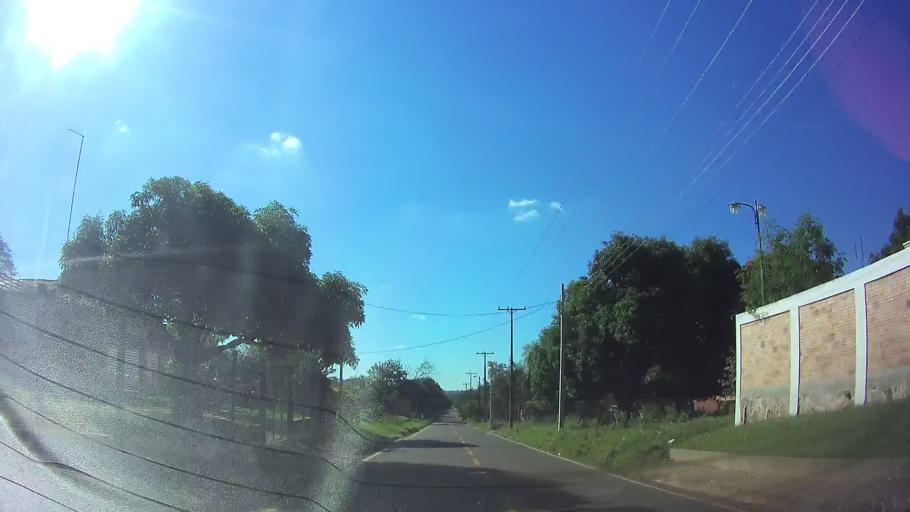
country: PY
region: Central
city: Limpio
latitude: -25.2000
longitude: -57.4784
